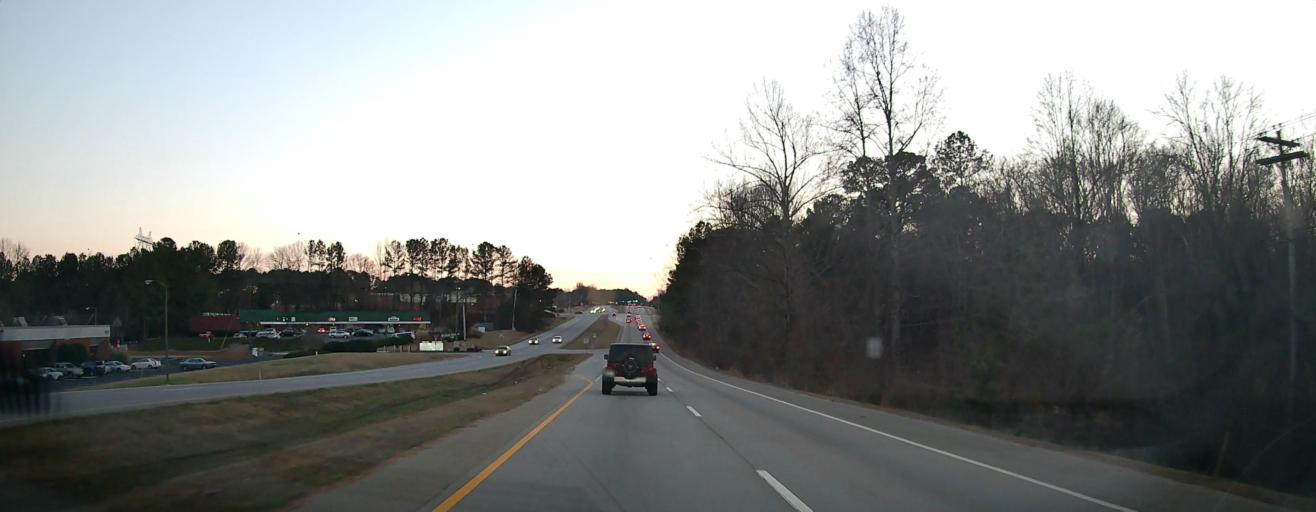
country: US
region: Georgia
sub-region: Fayette County
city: Fayetteville
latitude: 33.4862
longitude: -84.4339
